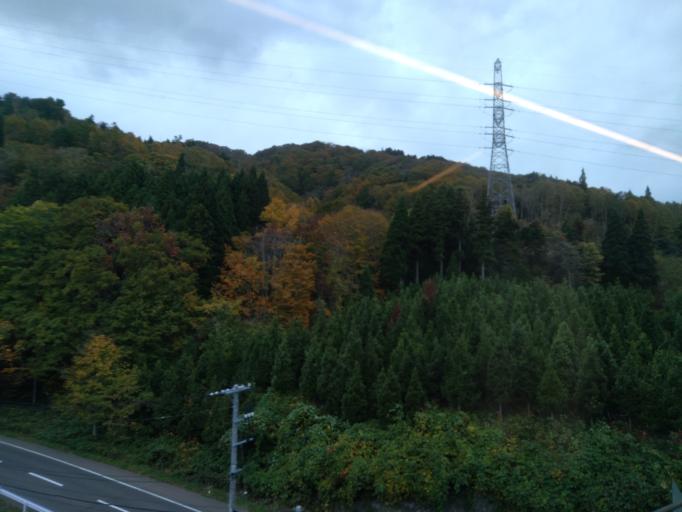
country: JP
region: Aomori
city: Goshogawara
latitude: 41.1514
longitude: 140.5099
